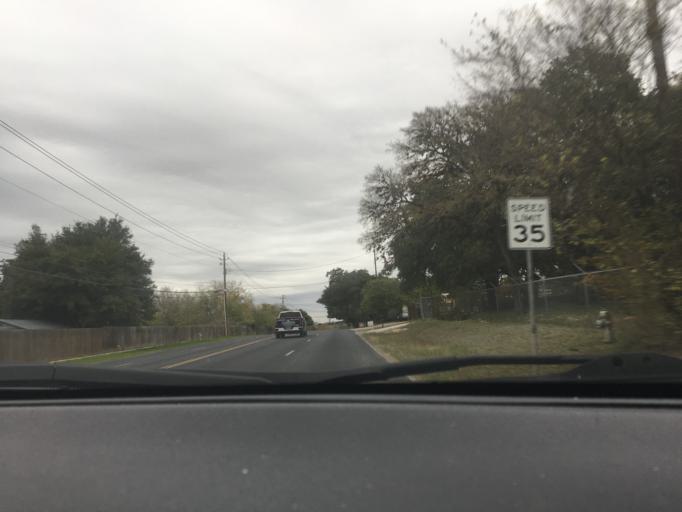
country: US
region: Texas
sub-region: Travis County
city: Onion Creek
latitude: 30.1770
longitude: -97.7975
